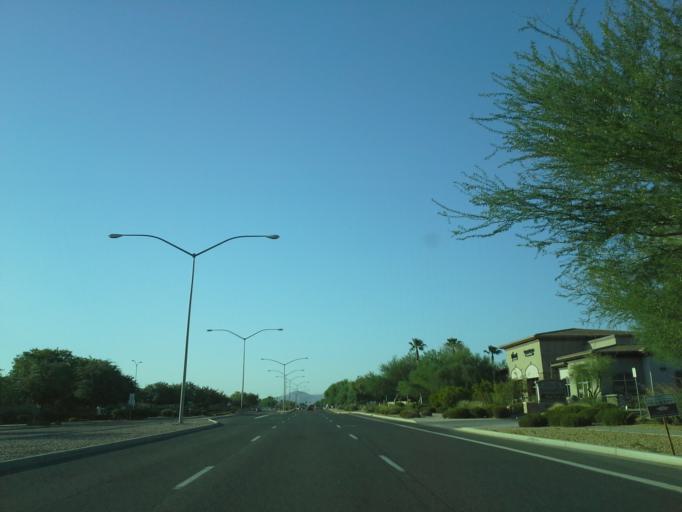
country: US
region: Arizona
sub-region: Pinal County
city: Apache Junction
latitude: 33.3592
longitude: -111.6358
